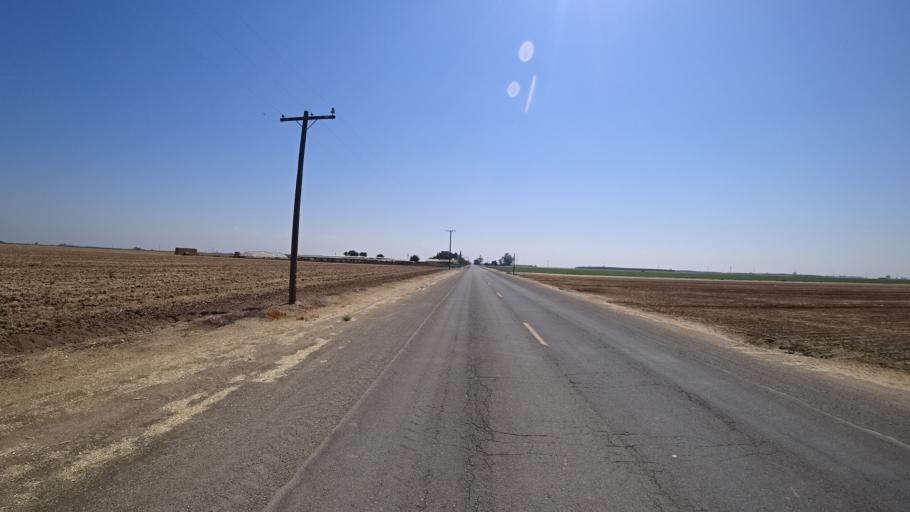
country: US
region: California
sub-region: Kings County
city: Hanford
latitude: 36.3720
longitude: -119.5710
